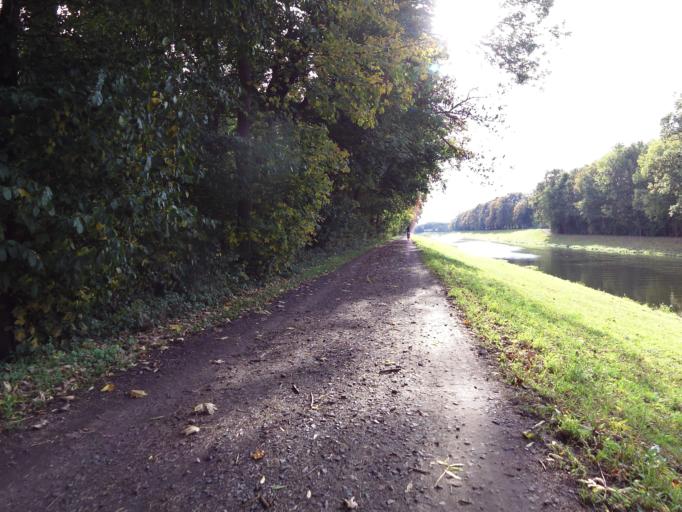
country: DE
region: Saxony
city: Leipzig
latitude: 51.3111
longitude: 12.3485
